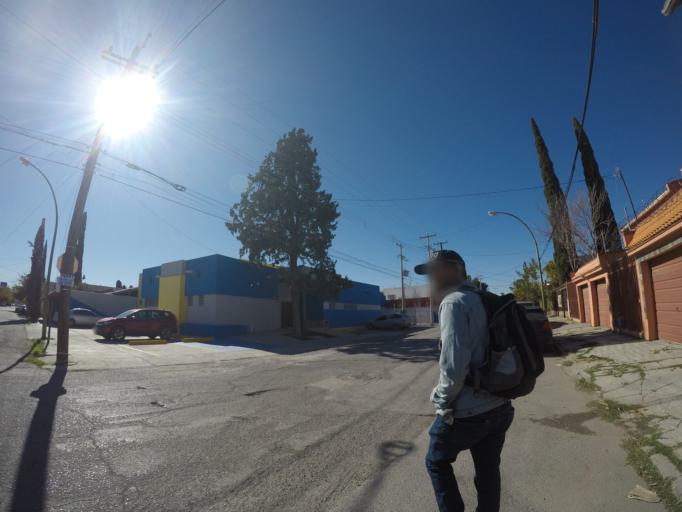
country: MX
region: Chihuahua
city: Ciudad Juarez
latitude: 31.7431
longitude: -106.4580
